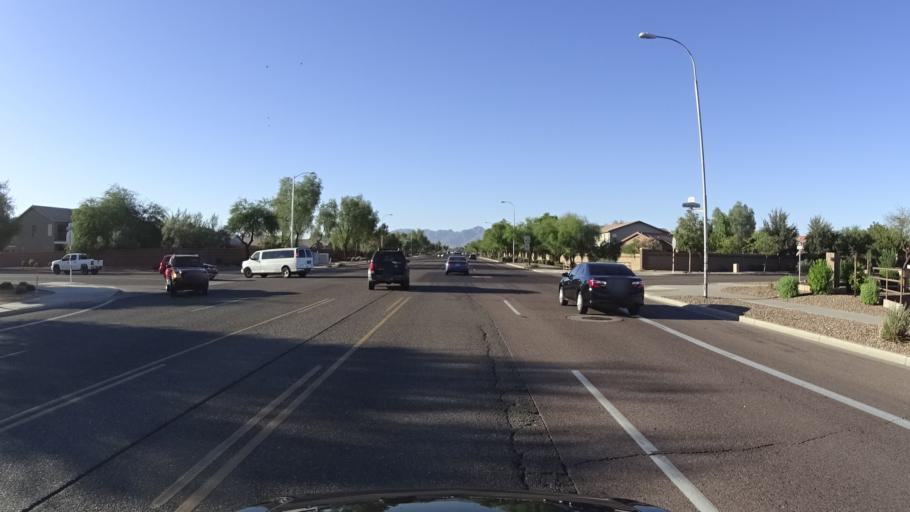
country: US
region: Arizona
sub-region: Maricopa County
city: Tolleson
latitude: 33.4305
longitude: -112.2385
